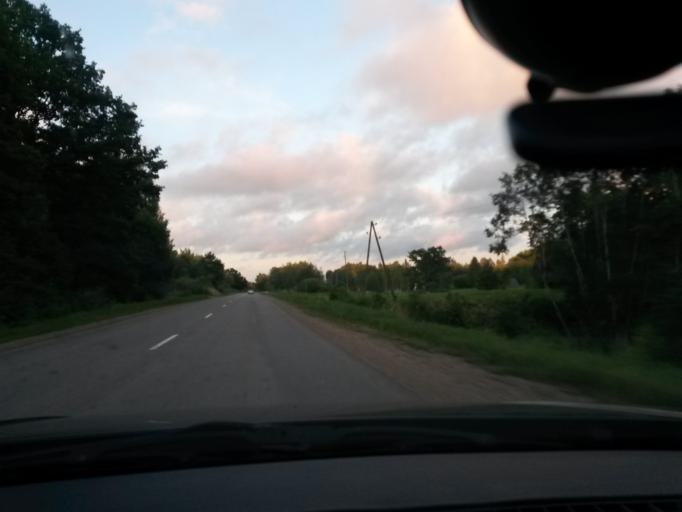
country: LV
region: Madonas Rajons
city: Madona
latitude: 56.8063
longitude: 26.0621
